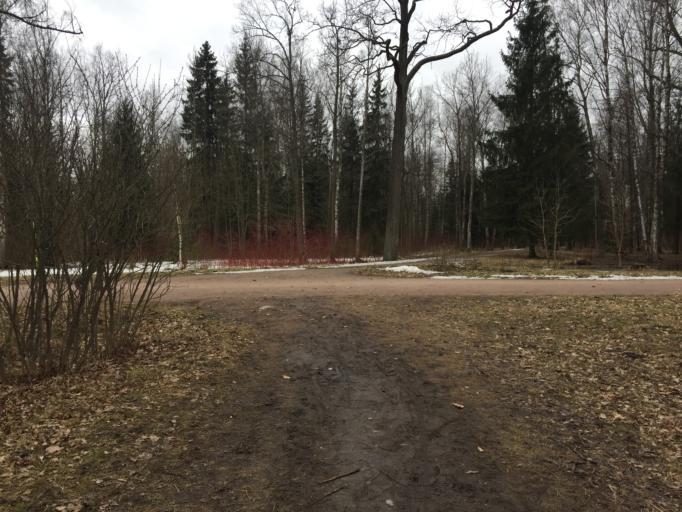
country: RU
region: St.-Petersburg
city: Pushkin
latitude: 59.7231
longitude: 30.3706
